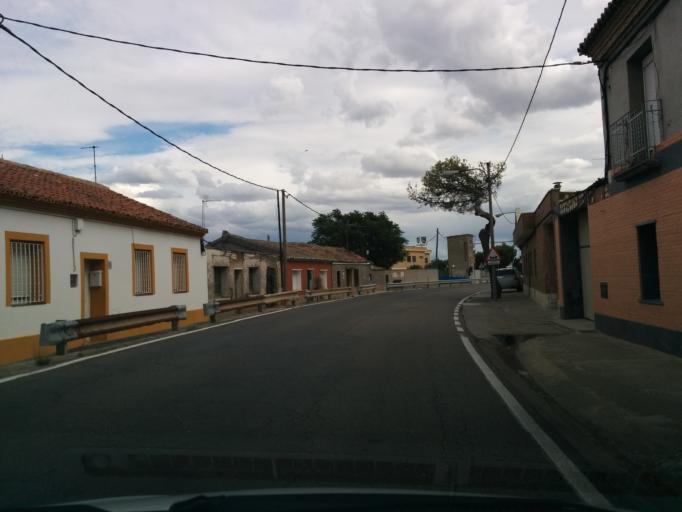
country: ES
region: Aragon
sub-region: Provincia de Zaragoza
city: Zaragoza
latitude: 41.6619
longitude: -0.8360
